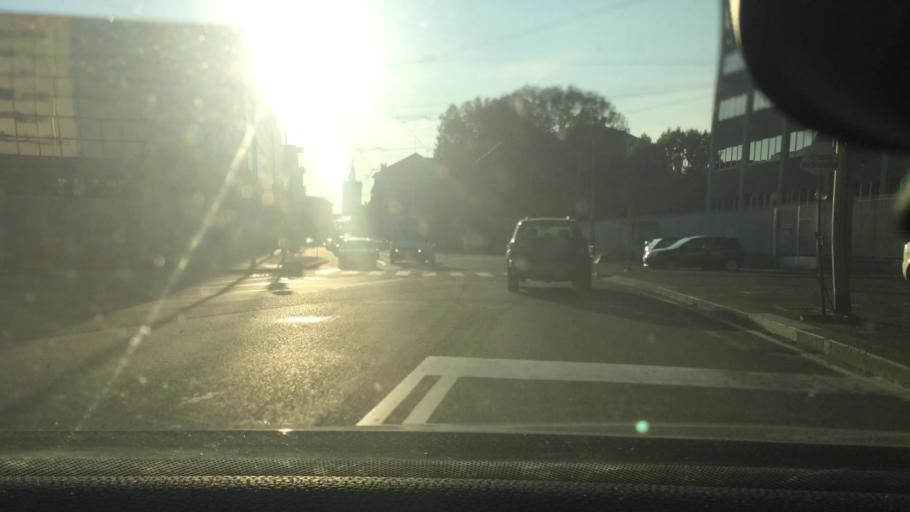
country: IT
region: Lombardy
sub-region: Citta metropolitana di Milano
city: Novate Milanese
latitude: 45.5081
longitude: 9.1369
